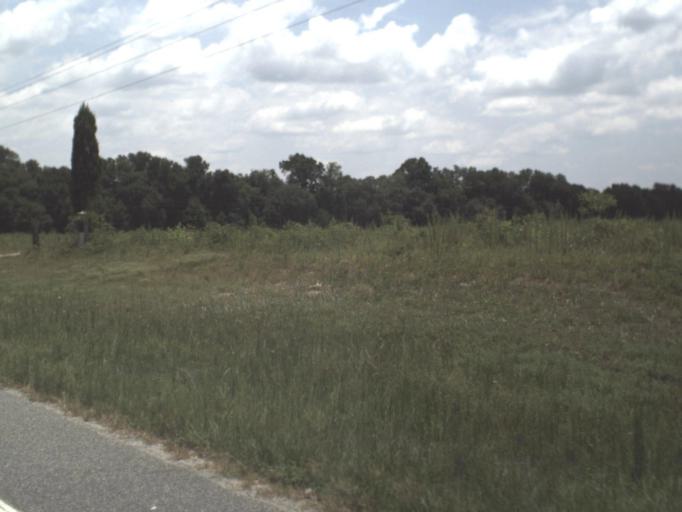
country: US
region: Florida
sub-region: Hamilton County
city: Jasper
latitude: 30.4902
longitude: -83.1176
